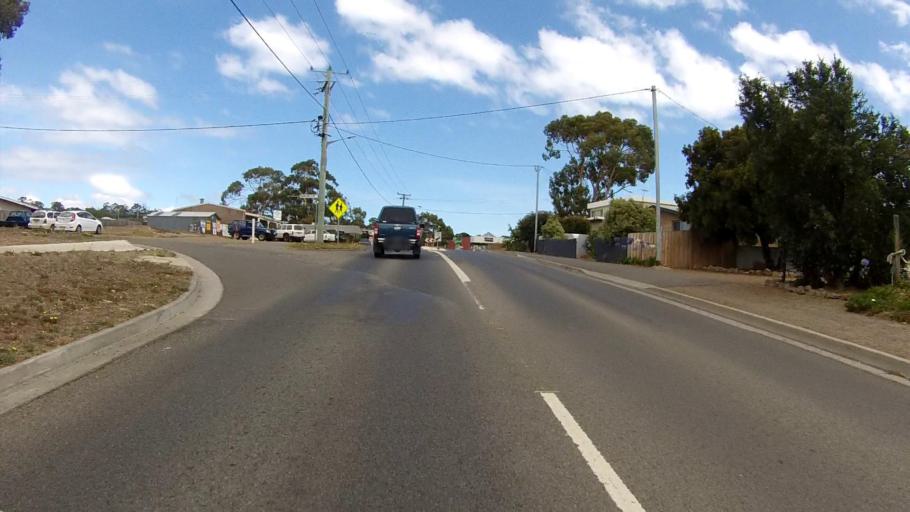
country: AU
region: Tasmania
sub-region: Sorell
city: Sorell
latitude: -42.8570
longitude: 147.6180
